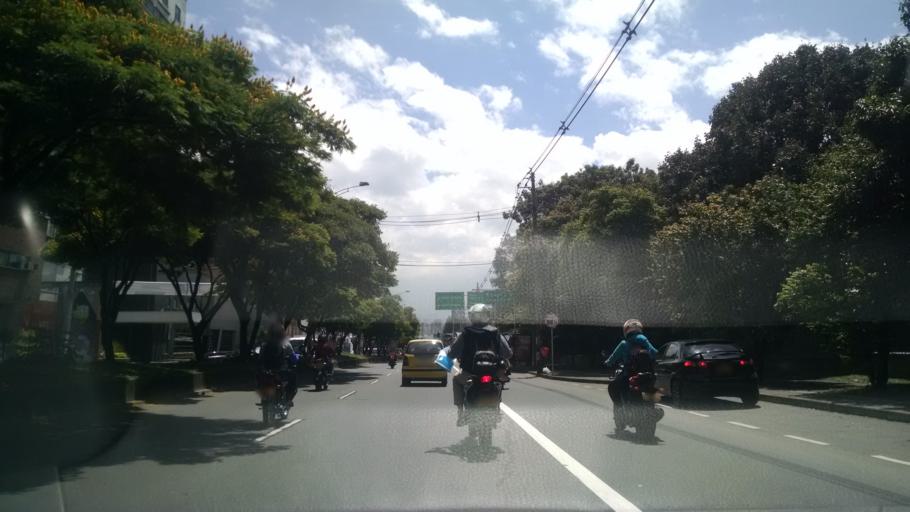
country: CO
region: Antioquia
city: Medellin
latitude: 6.2592
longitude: -75.5877
